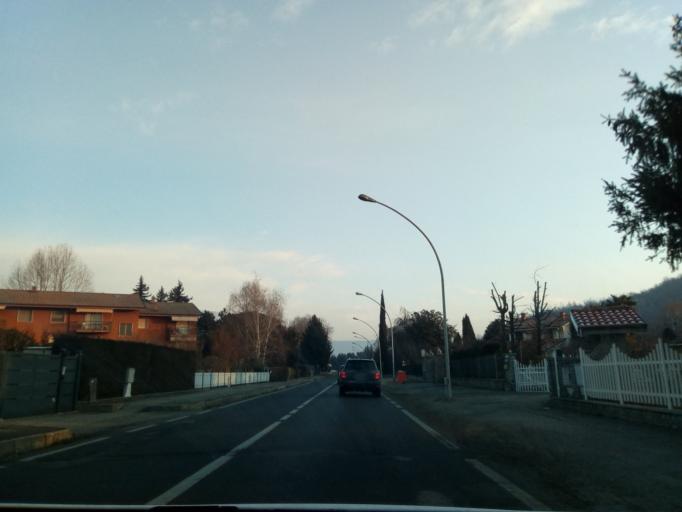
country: IT
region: Piedmont
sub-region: Provincia di Torino
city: Pavone Canavese
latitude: 45.4404
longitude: 7.8512
